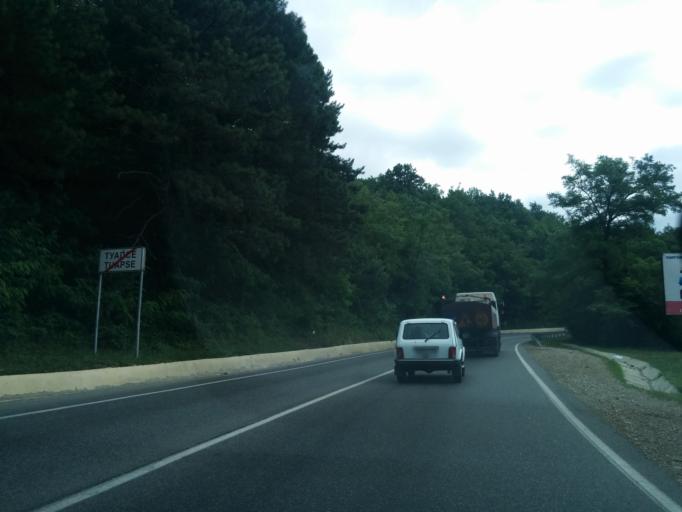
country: RU
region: Krasnodarskiy
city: Agoy
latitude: 44.1207
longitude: 39.0488
